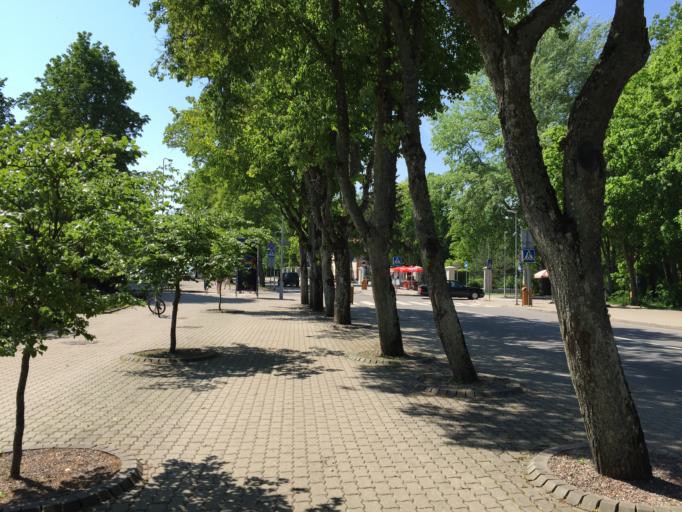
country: LT
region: Klaipedos apskritis
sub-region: Klaipeda
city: Palanga
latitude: 55.9110
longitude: 21.0628
